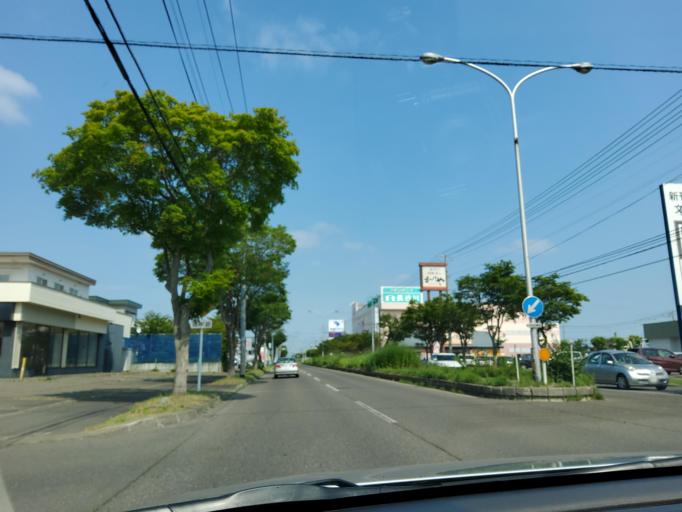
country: JP
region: Hokkaido
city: Obihiro
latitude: 42.9173
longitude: 143.1382
